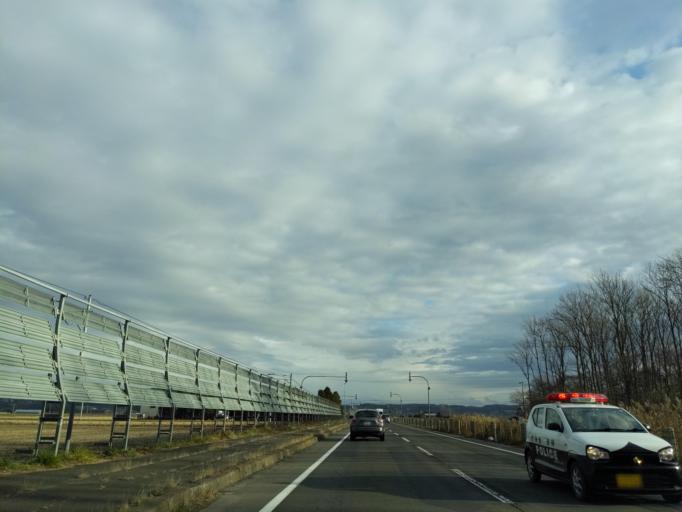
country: JP
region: Hokkaido
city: Kitahiroshima
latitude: 42.9610
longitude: 141.6875
